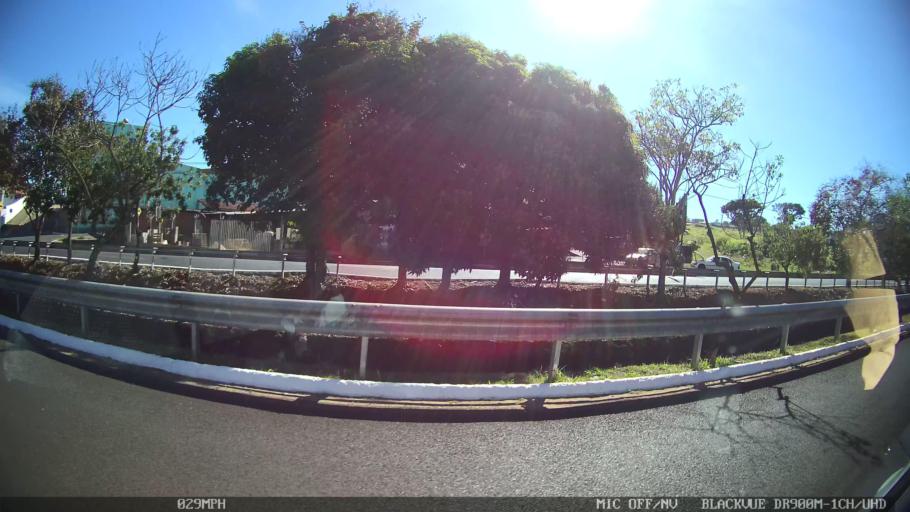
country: BR
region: Sao Paulo
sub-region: Franca
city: Franca
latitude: -20.5199
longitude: -47.3876
